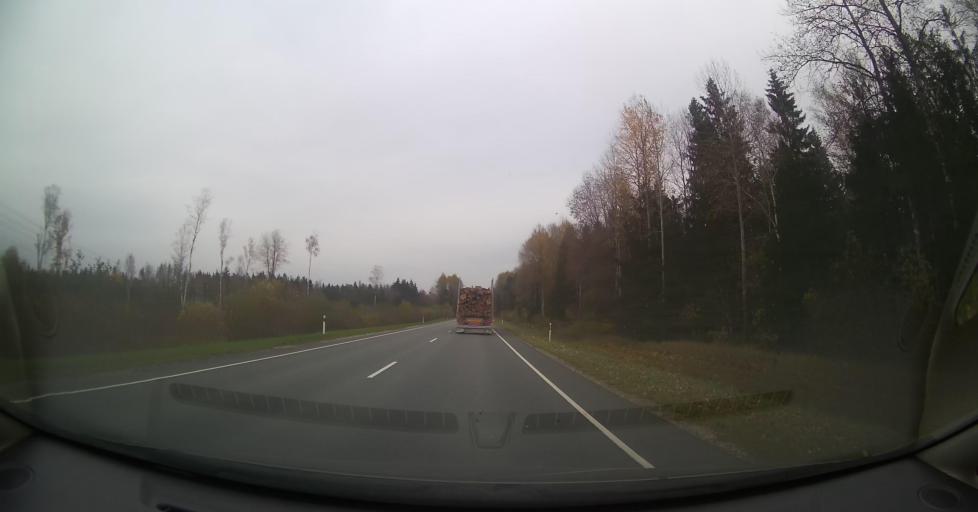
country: EE
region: Harju
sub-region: Nissi vald
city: Turba
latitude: 59.0742
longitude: 24.2080
